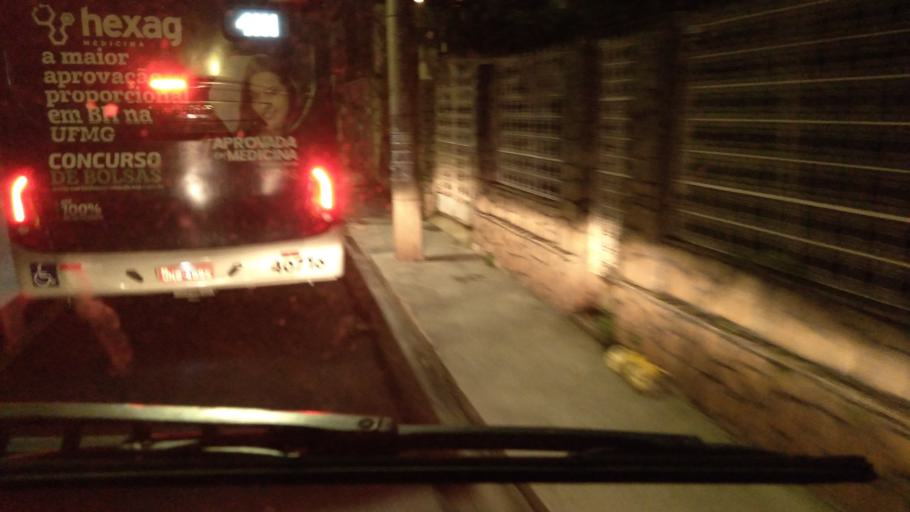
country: BR
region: Minas Gerais
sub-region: Belo Horizonte
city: Belo Horizonte
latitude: -19.9108
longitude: -43.9610
